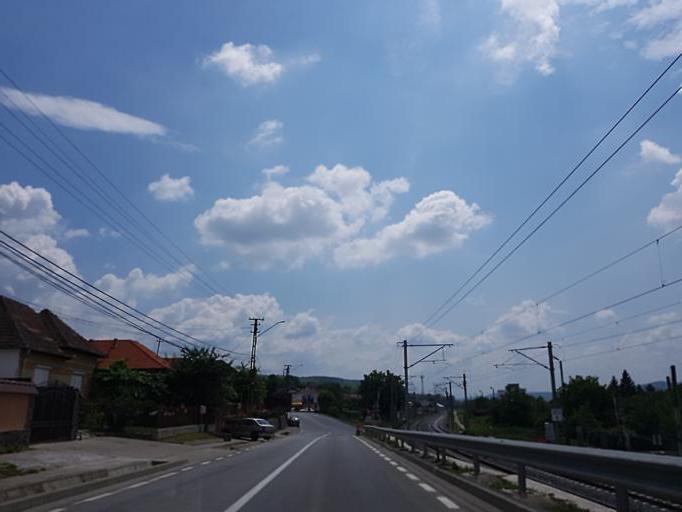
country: RO
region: Alba
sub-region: Municipiul Blaj
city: Veza
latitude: 46.1753
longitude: 23.9359
